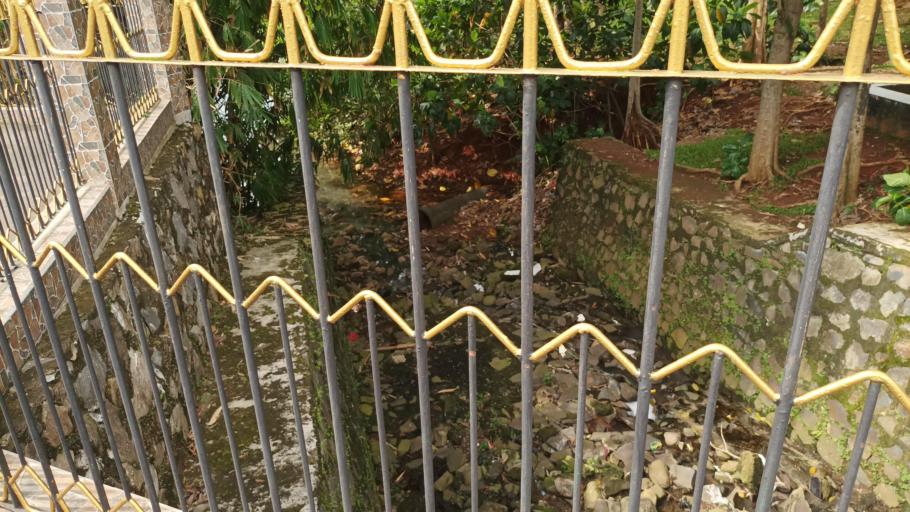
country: ID
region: West Java
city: Depok
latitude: -6.4347
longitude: 106.8419
